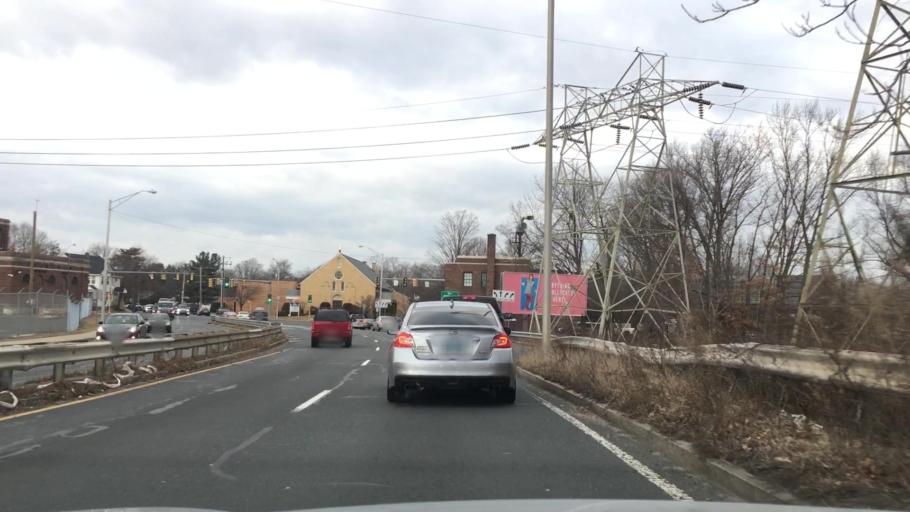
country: US
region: Massachusetts
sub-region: Hampden County
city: Springfield
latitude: 42.1433
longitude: -72.5506
